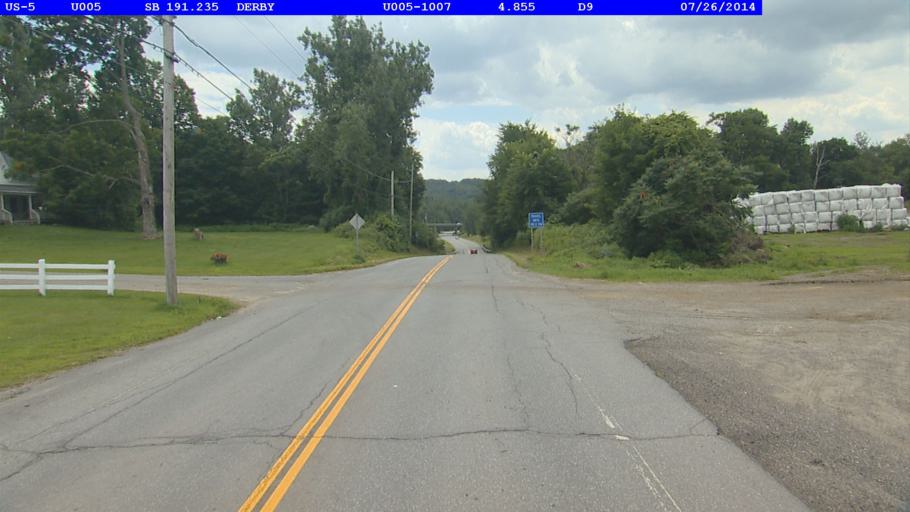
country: US
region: Vermont
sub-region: Orleans County
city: Newport
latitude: 44.9913
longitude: -72.1065
